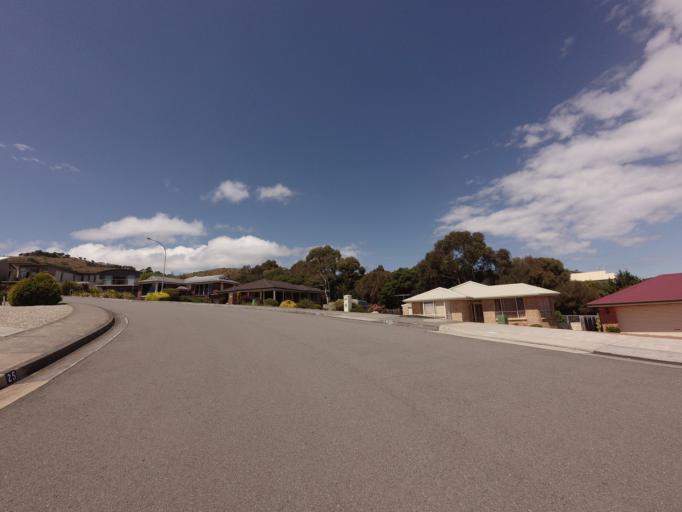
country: AU
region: Tasmania
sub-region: Clarence
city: Howrah
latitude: -42.9205
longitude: 147.4118
